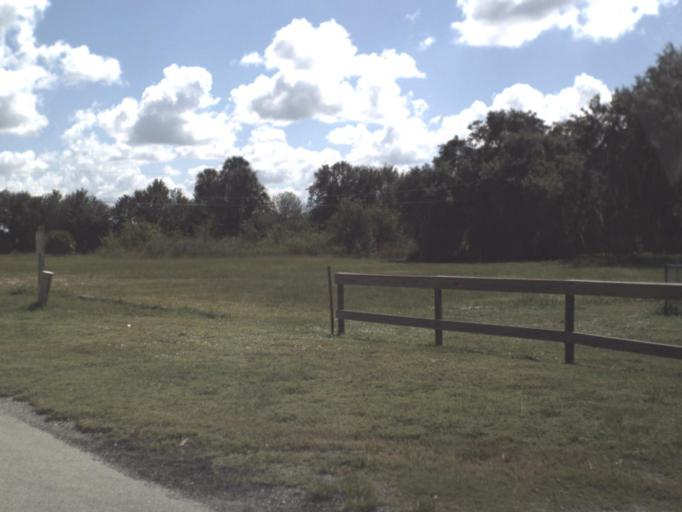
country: US
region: Florida
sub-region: Okeechobee County
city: Taylor Creek
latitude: 27.1962
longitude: -80.7665
